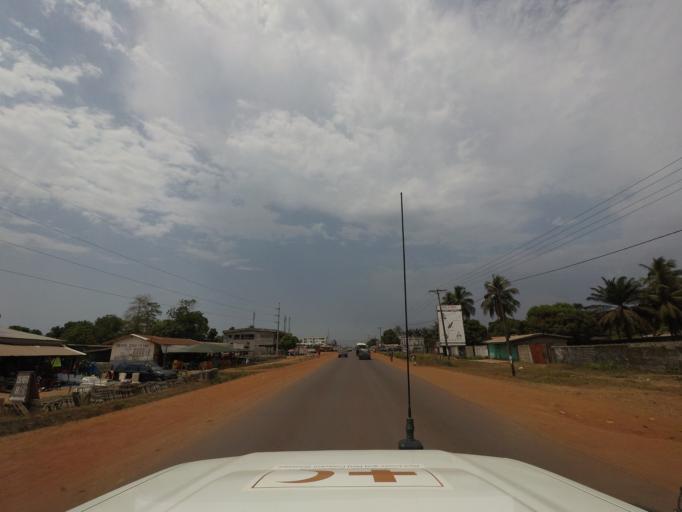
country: LR
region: Montserrado
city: Monrovia
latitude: 6.2823
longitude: -10.6918
